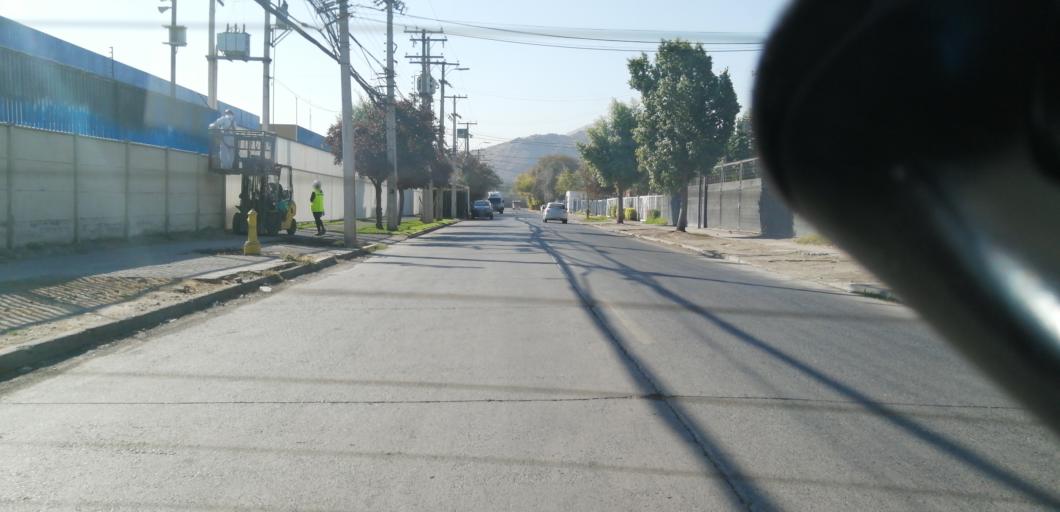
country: CL
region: Santiago Metropolitan
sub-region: Provincia de Santiago
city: Lo Prado
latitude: -33.3768
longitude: -70.7528
